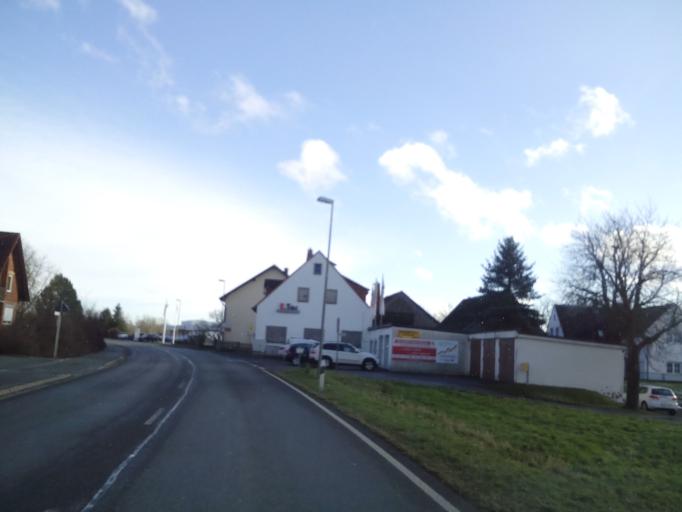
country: DE
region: Bavaria
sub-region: Upper Franconia
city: Mainleus
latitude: 50.1154
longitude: 11.3437
